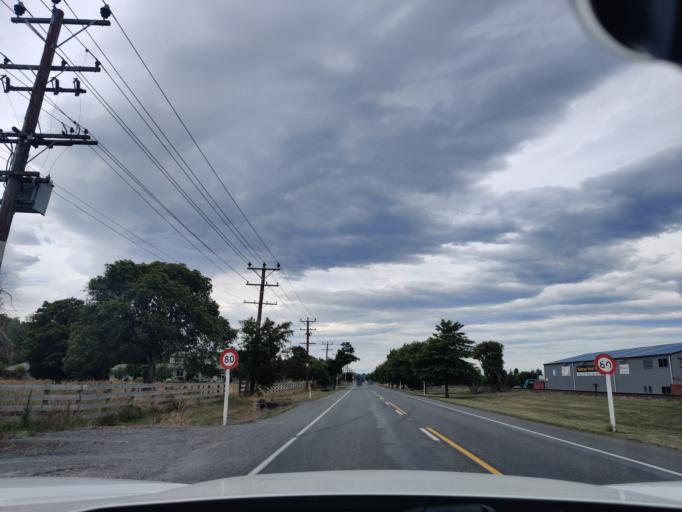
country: NZ
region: Wellington
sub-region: Masterton District
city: Masterton
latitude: -40.9563
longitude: 175.6180
